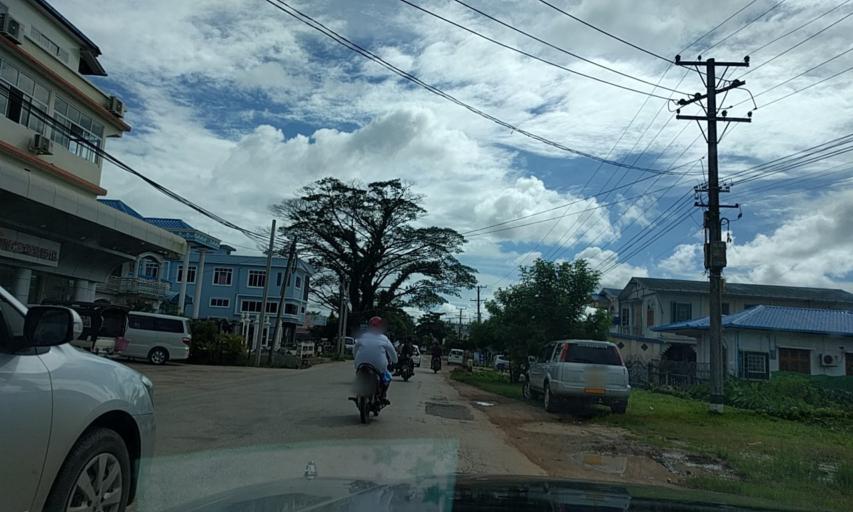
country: MM
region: Mon
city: Mawlamyine
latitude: 16.4601
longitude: 97.6479
